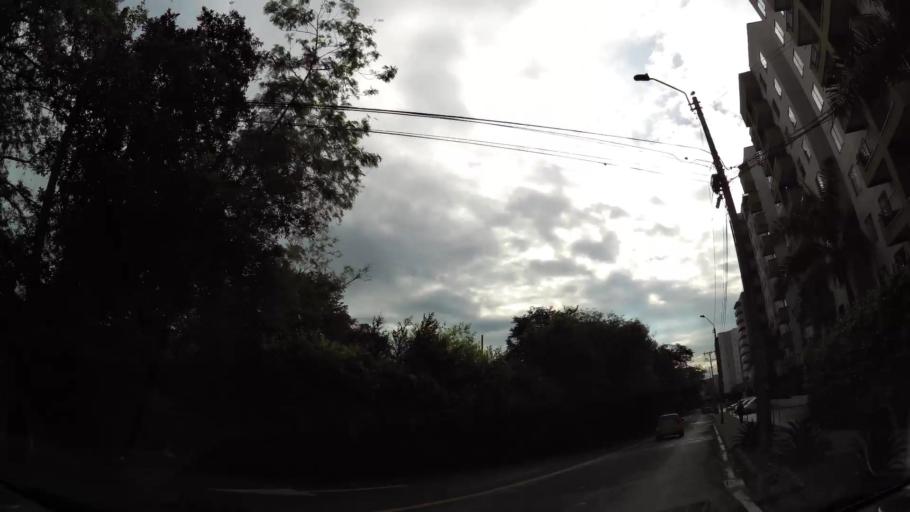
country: CO
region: Valle del Cauca
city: Cali
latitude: 3.4929
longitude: -76.5212
